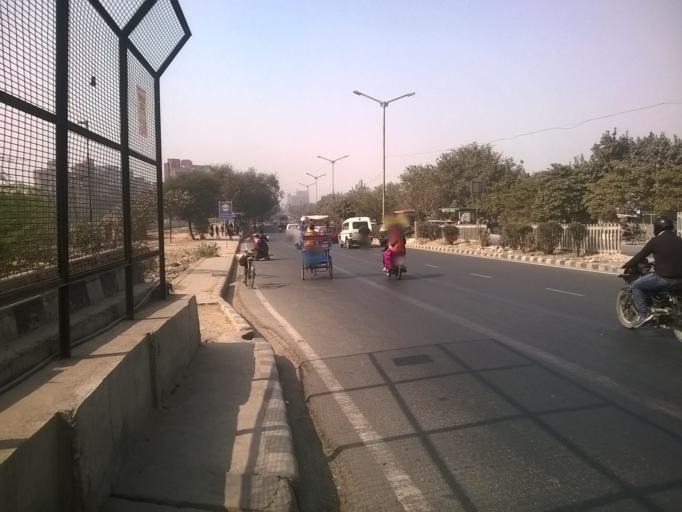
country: IN
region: NCT
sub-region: West Delhi
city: Nangloi Jat
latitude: 28.5994
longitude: 77.0619
